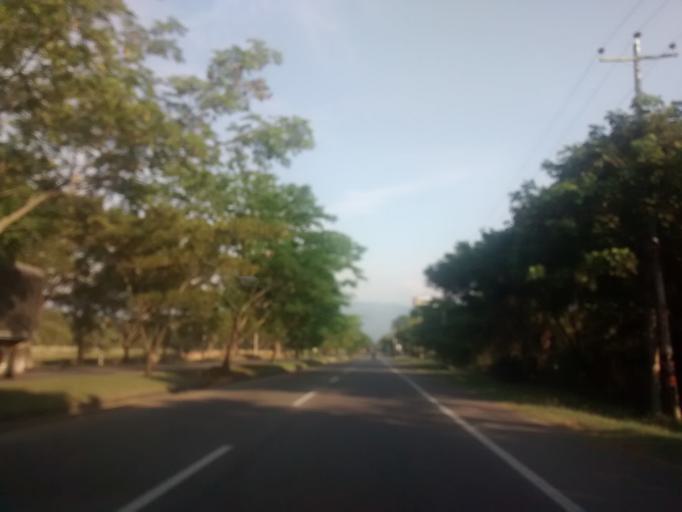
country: CO
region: Tolima
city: Melgar
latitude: 4.2268
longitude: -74.7001
